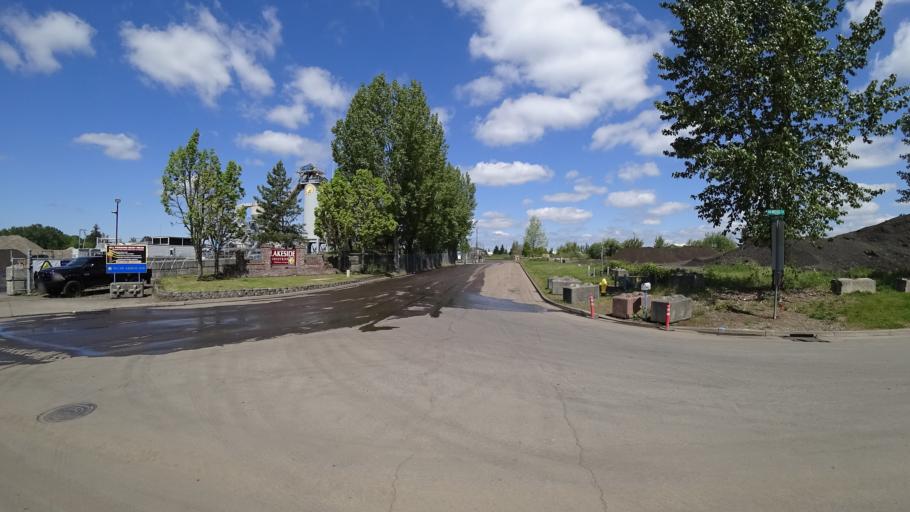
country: US
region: Oregon
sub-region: Washington County
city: Hillsboro
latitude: 45.5125
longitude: -123.0012
